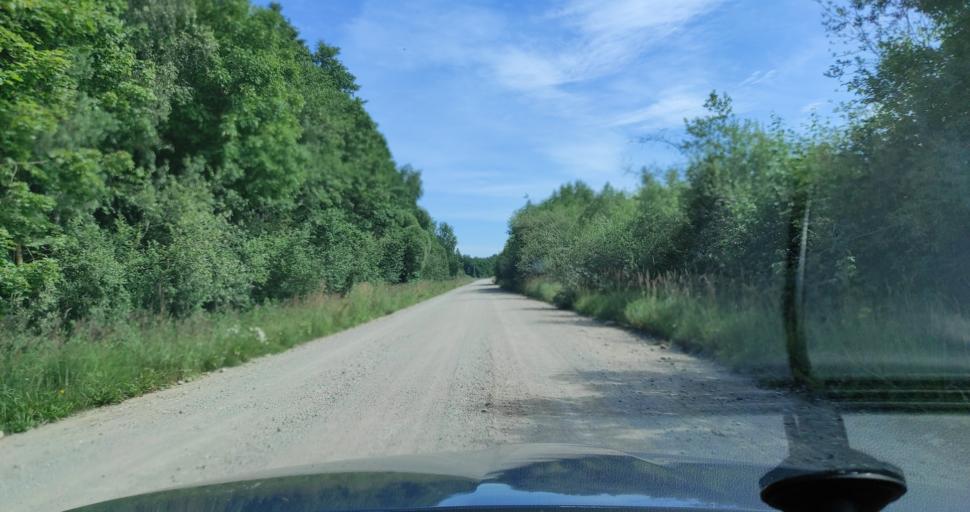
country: LV
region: Durbe
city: Liegi
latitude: 56.7522
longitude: 21.3581
